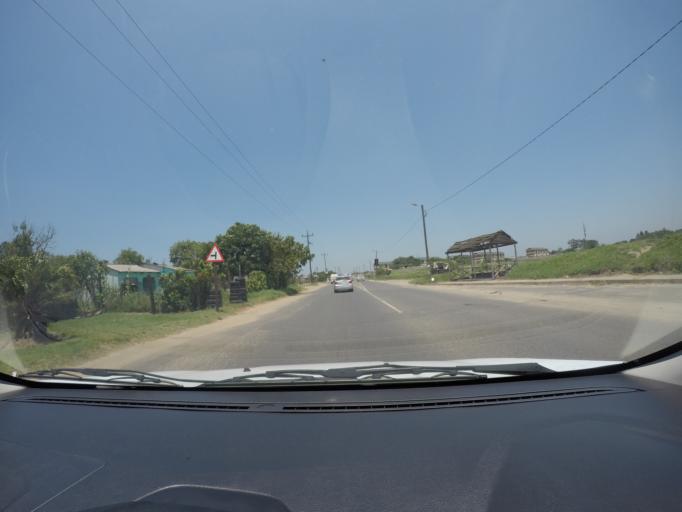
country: ZA
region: KwaZulu-Natal
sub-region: uThungulu District Municipality
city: eSikhawini
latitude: -28.8812
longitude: 31.9068
